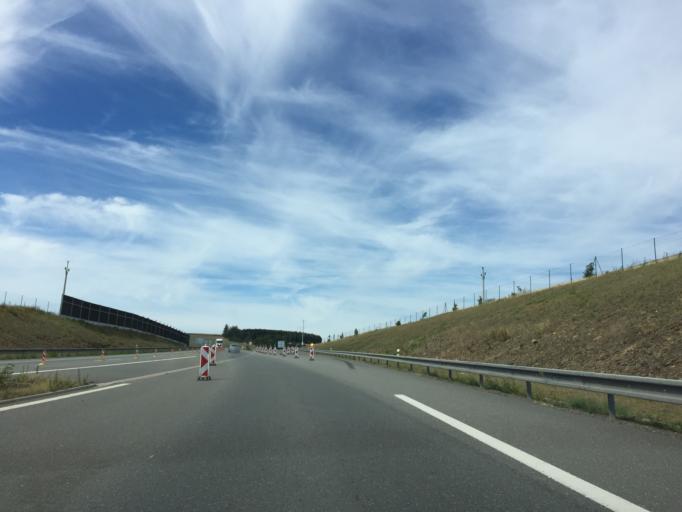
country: CZ
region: Jihocesky
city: Chotoviny
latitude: 49.5422
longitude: 14.6655
